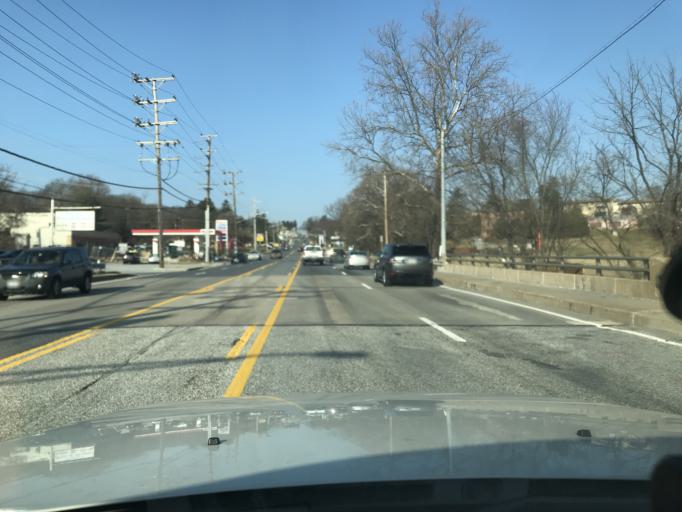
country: US
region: Maryland
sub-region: Baltimore County
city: Owings Mills
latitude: 39.4208
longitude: -76.7817
